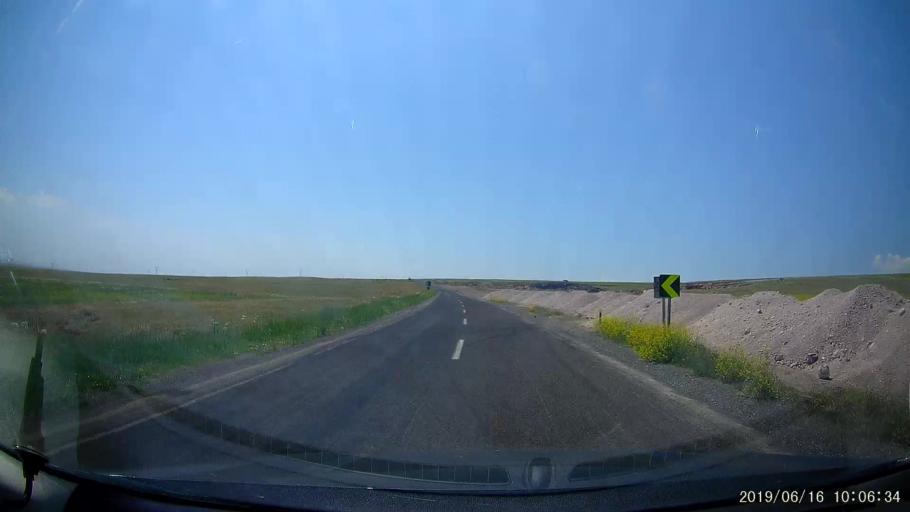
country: TR
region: Kars
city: Digor
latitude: 40.2537
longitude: 43.5436
